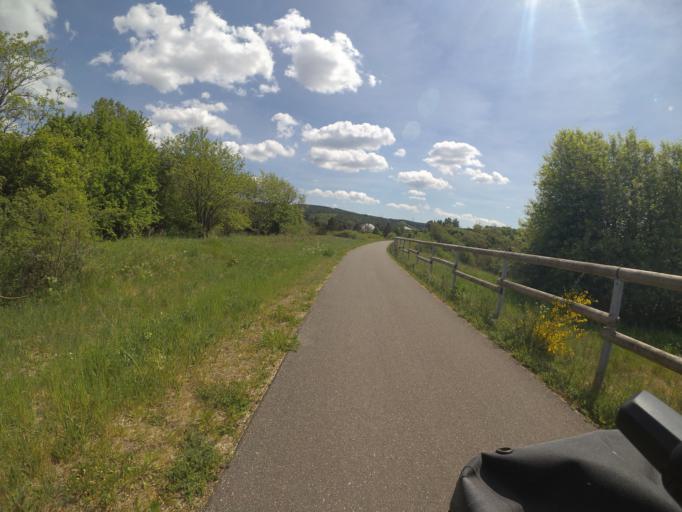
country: DE
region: Rheinland-Pfalz
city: Hallschlag
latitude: 50.3545
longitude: 6.4322
